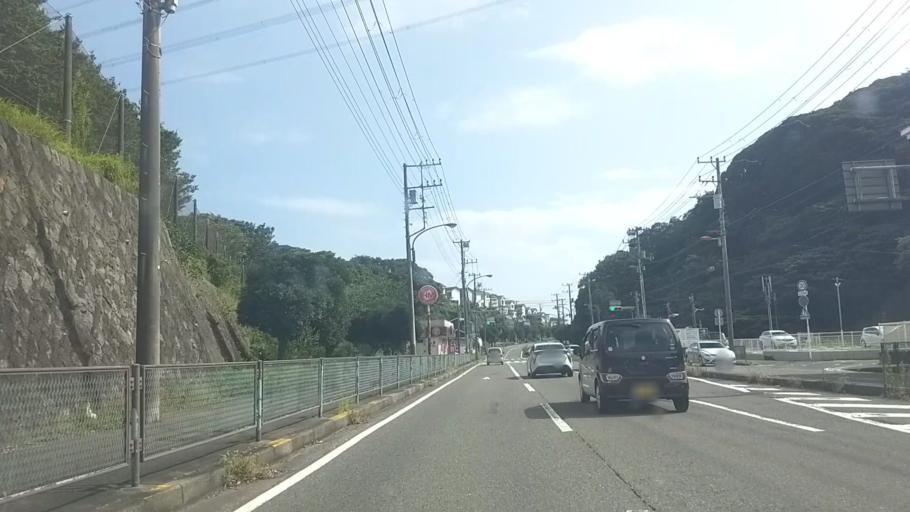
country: JP
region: Kanagawa
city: Yokosuka
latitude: 35.2239
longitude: 139.6845
